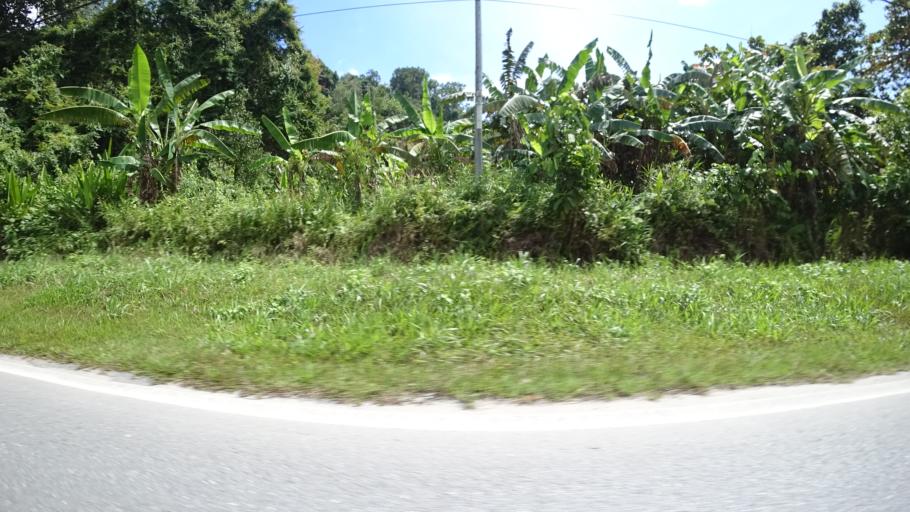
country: MY
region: Sarawak
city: Limbang
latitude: 4.6835
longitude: 114.9816
